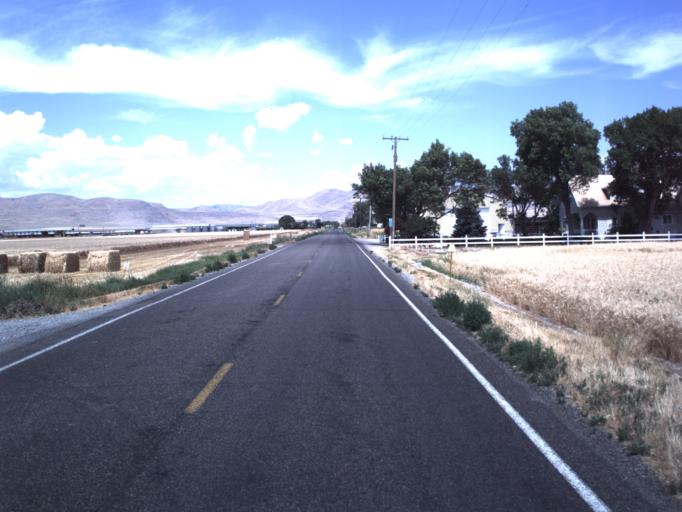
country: US
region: Utah
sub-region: Box Elder County
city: Tremonton
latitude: 41.7018
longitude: -112.2779
